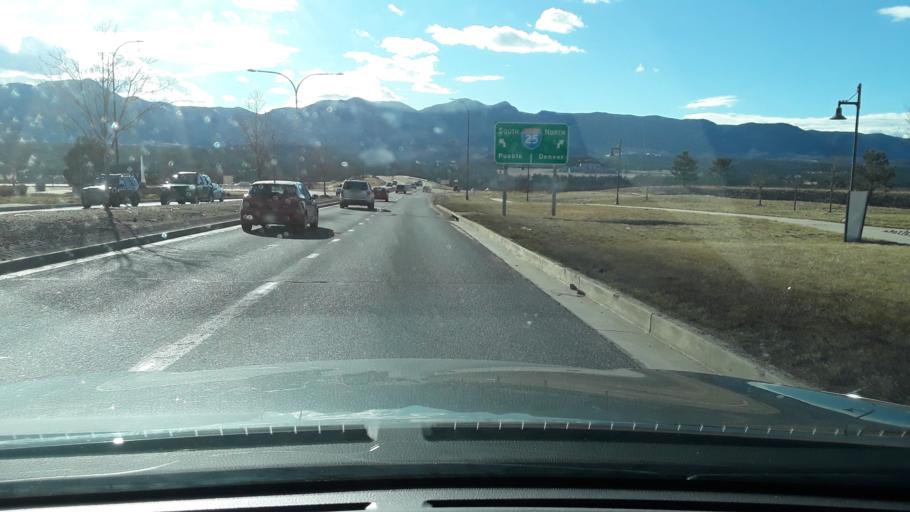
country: US
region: Colorado
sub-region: El Paso County
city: Air Force Academy
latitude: 38.9910
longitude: -104.8096
